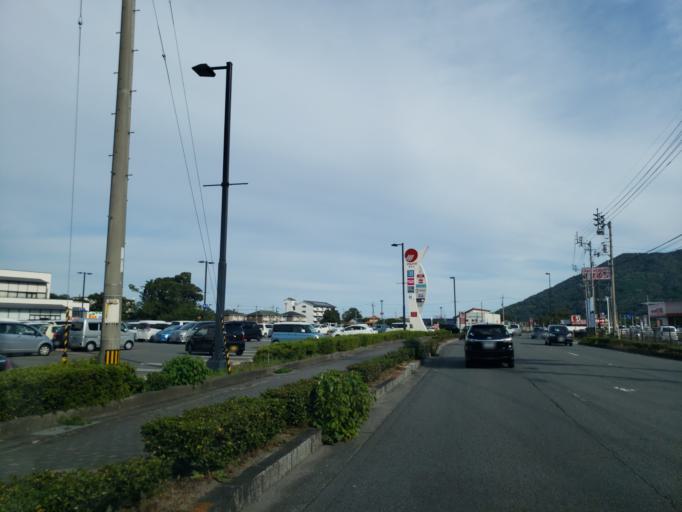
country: JP
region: Tokushima
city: Wakimachi
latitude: 34.0635
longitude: 134.1652
